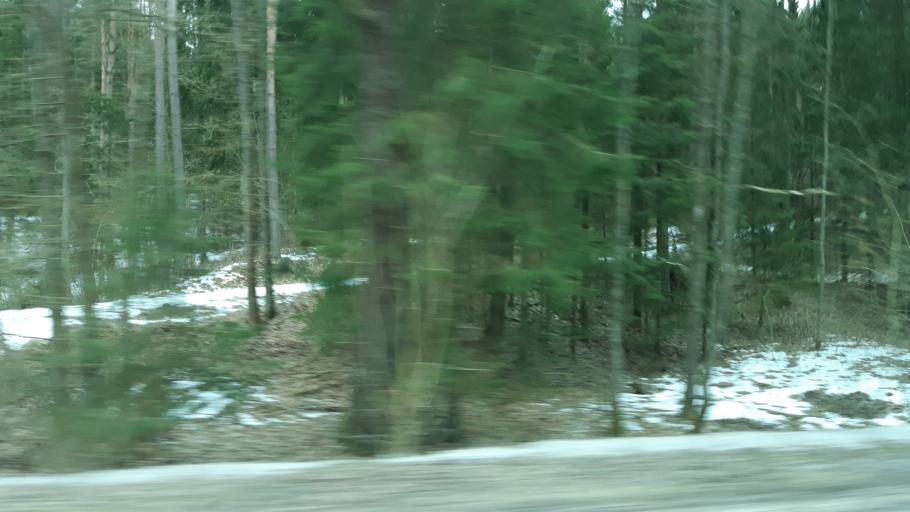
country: PL
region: Podlasie
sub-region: Suwalki
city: Suwalki
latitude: 54.2915
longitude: 22.9562
